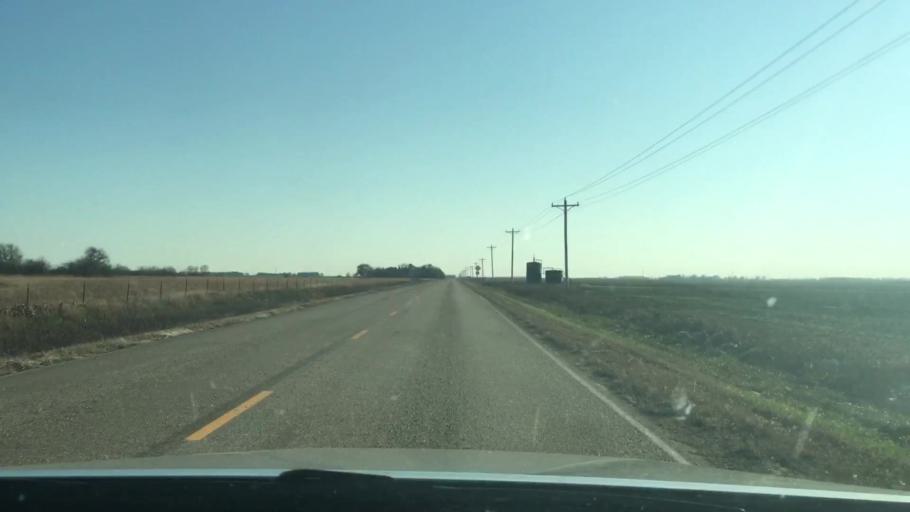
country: US
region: Kansas
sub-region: Reno County
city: Nickerson
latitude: 38.2381
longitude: -98.0878
